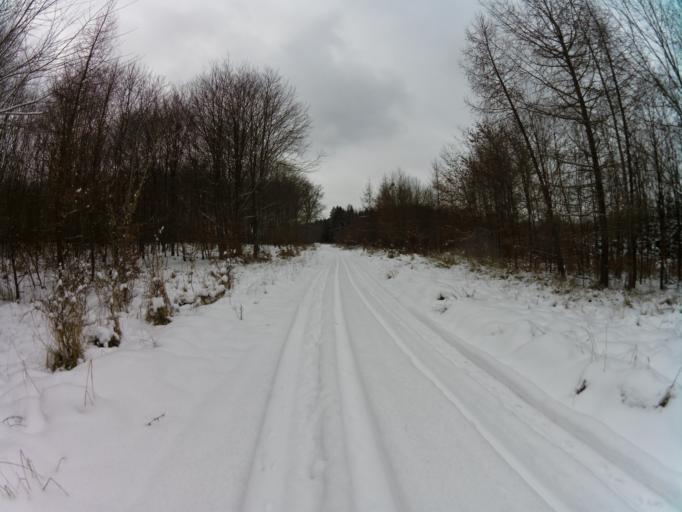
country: PL
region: West Pomeranian Voivodeship
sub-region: Powiat choszczenski
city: Recz
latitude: 53.3263
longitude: 15.5408
